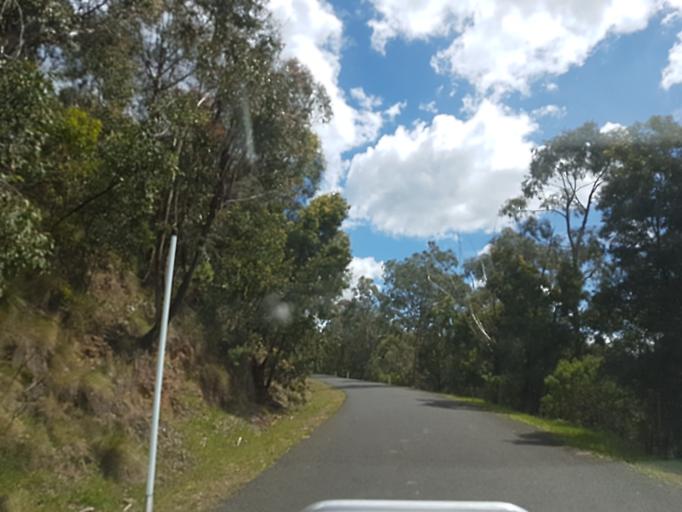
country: AU
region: Victoria
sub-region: East Gippsland
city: Bairnsdale
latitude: -37.4160
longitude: 147.2520
